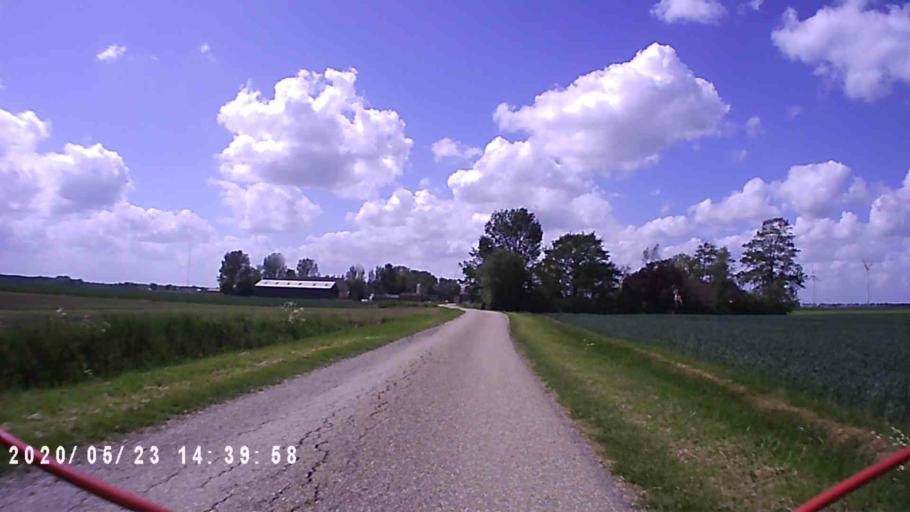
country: NL
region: Groningen
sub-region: Gemeente Delfzijl
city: Delfzijl
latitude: 53.2717
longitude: 6.9732
